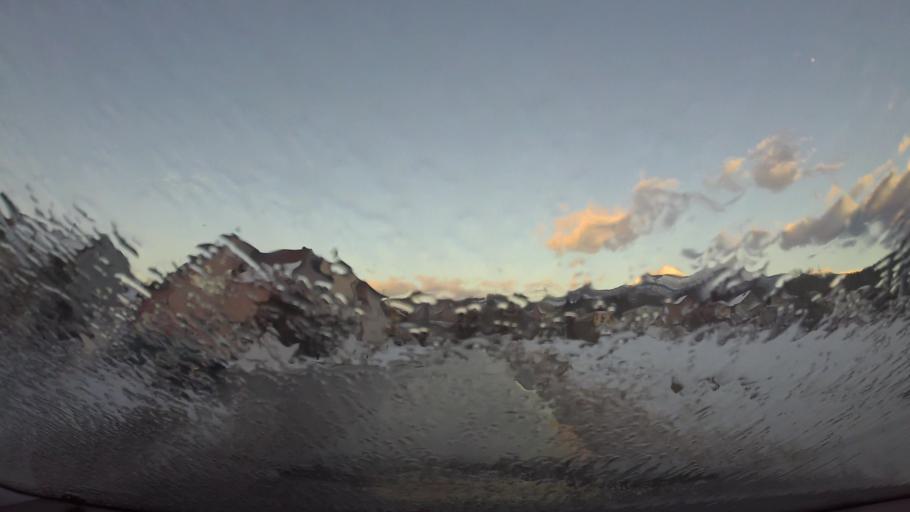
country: BA
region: Federation of Bosnia and Herzegovina
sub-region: Kanton Sarajevo
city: Sarajevo
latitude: 43.8066
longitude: 18.3742
